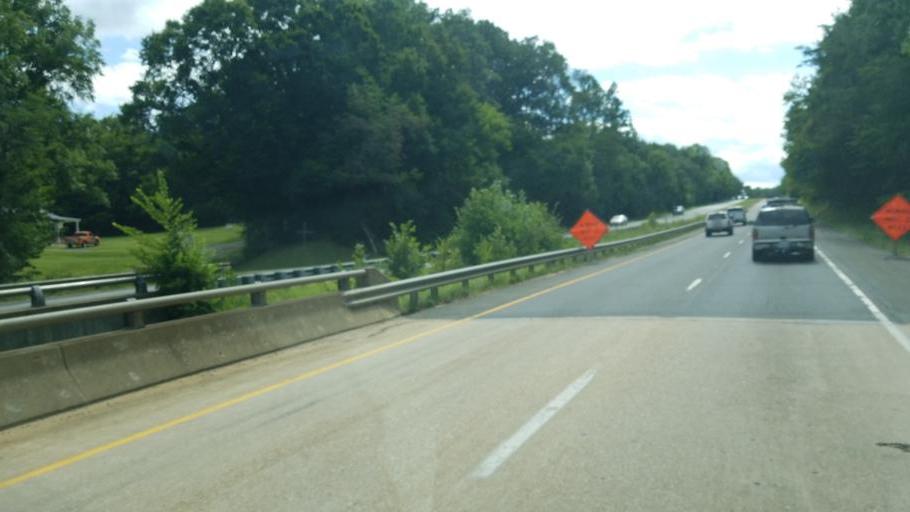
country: US
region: Virginia
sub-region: Stafford County
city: Falmouth
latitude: 38.4301
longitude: -77.6290
